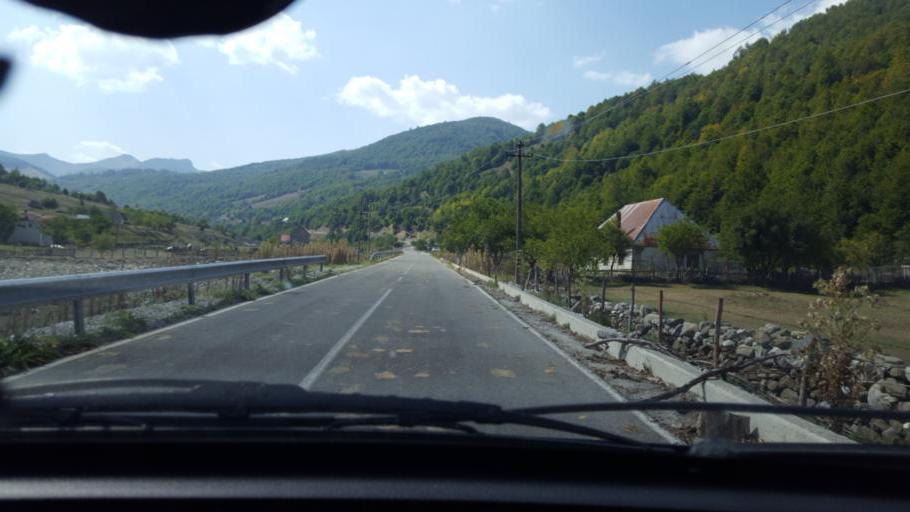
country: ME
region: Andrijevica
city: Andrijevica
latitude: 42.5559
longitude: 19.7287
